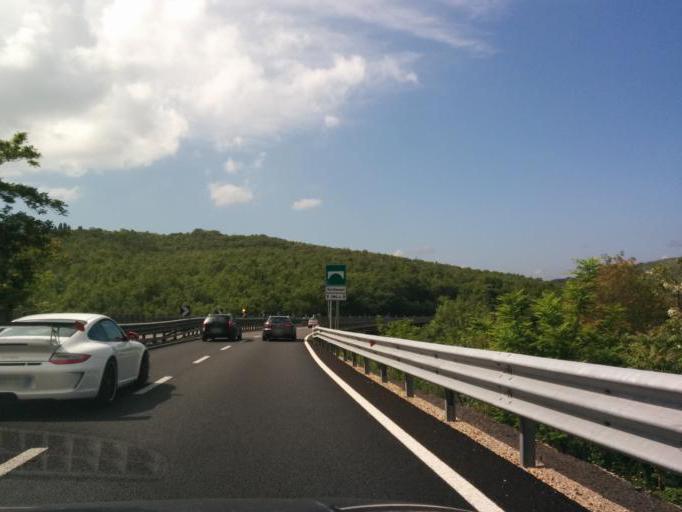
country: IT
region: Tuscany
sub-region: Province of Florence
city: Barberino Val d'Elsa
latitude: 43.5165
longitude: 11.1969
